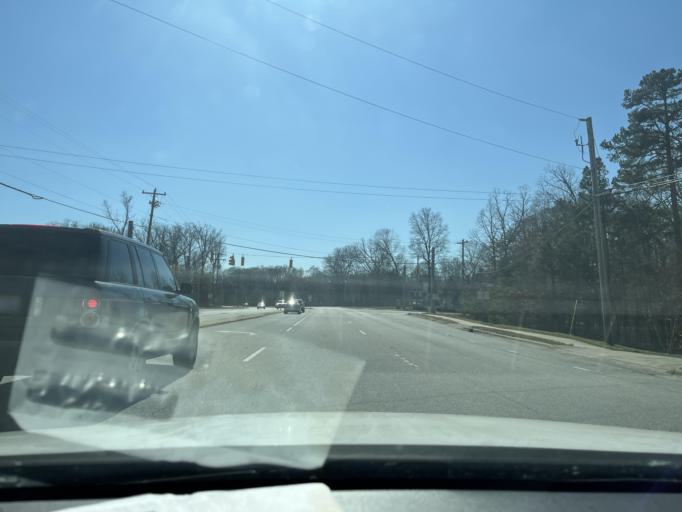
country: US
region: North Carolina
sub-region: Guilford County
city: Jamestown
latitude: 36.0220
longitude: -79.9259
